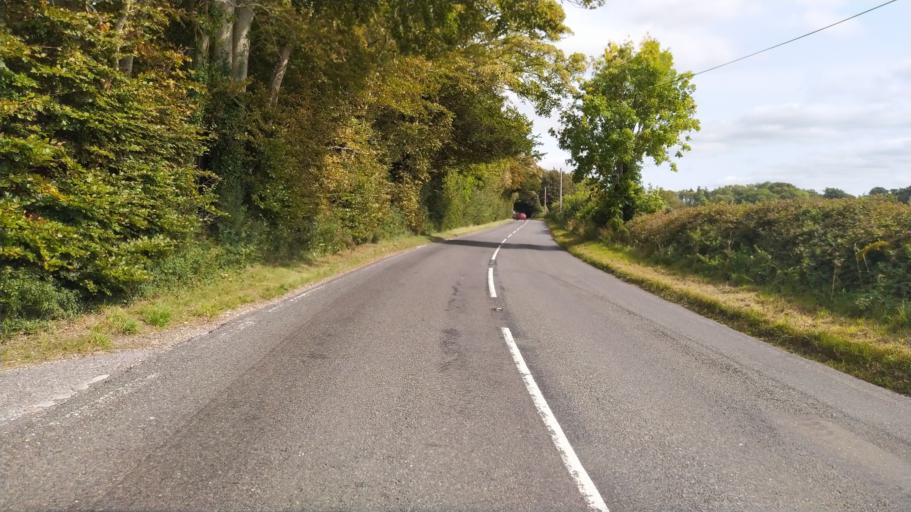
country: GB
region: England
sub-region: Dorset
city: Three Legged Cross
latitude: 50.8951
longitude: -1.9529
